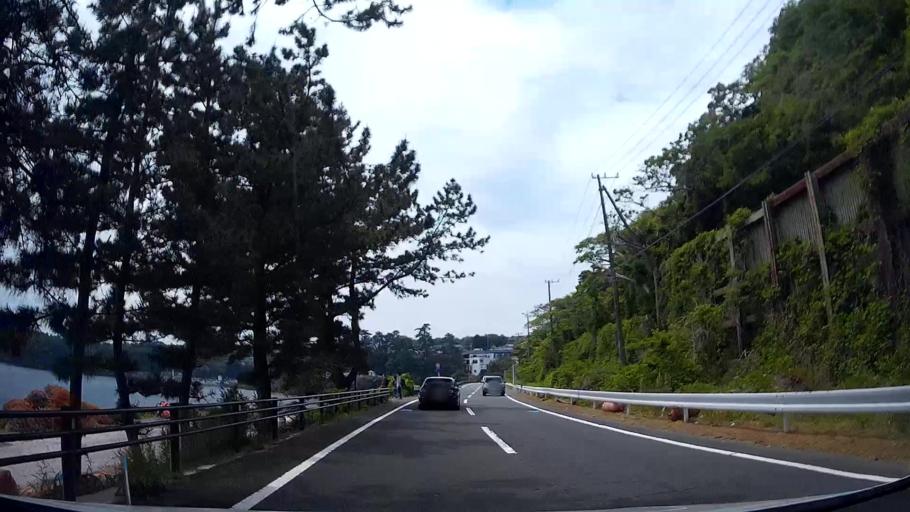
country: JP
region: Shizuoka
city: Ito
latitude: 34.9006
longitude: 139.1327
